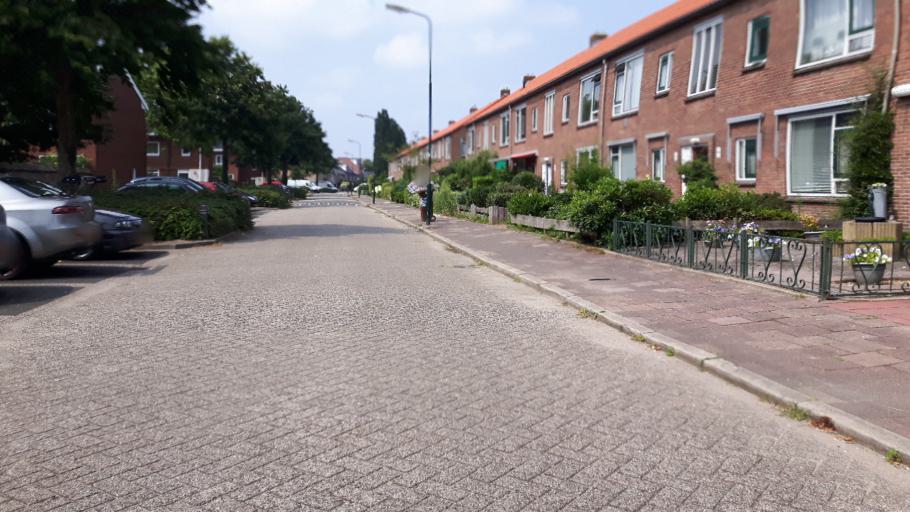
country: NL
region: Utrecht
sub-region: Gemeente Zeist
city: Zeist
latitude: 52.1165
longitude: 5.2839
